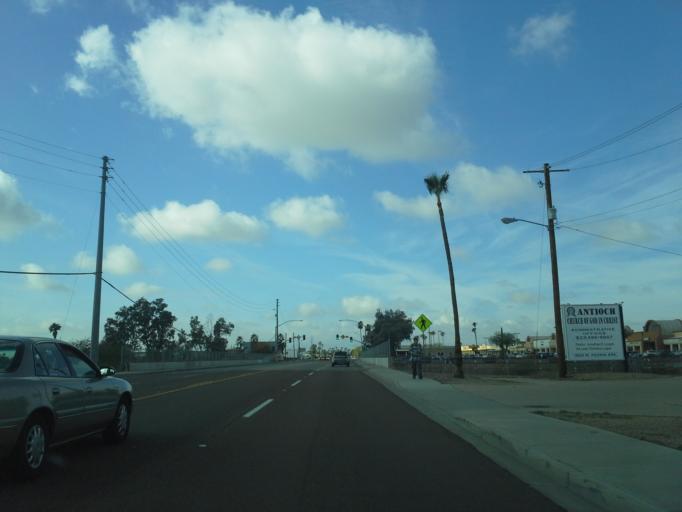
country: US
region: Arizona
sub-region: Maricopa County
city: Sun City
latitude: 33.5806
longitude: -112.2665
